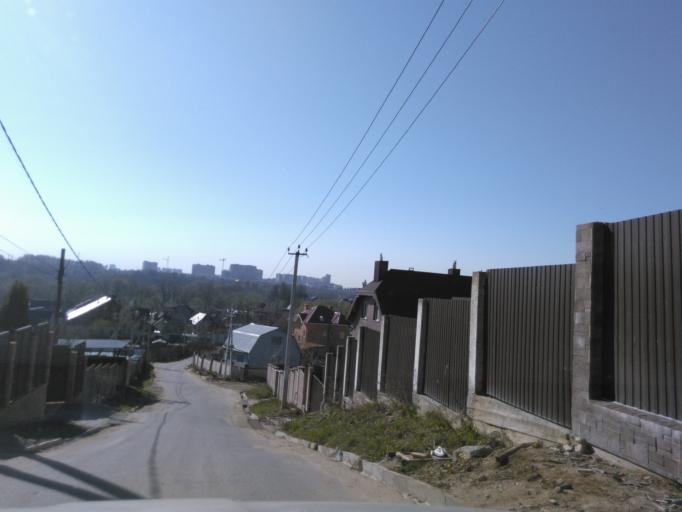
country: RU
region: Moscow
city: Khimki
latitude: 55.8790
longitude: 37.3741
